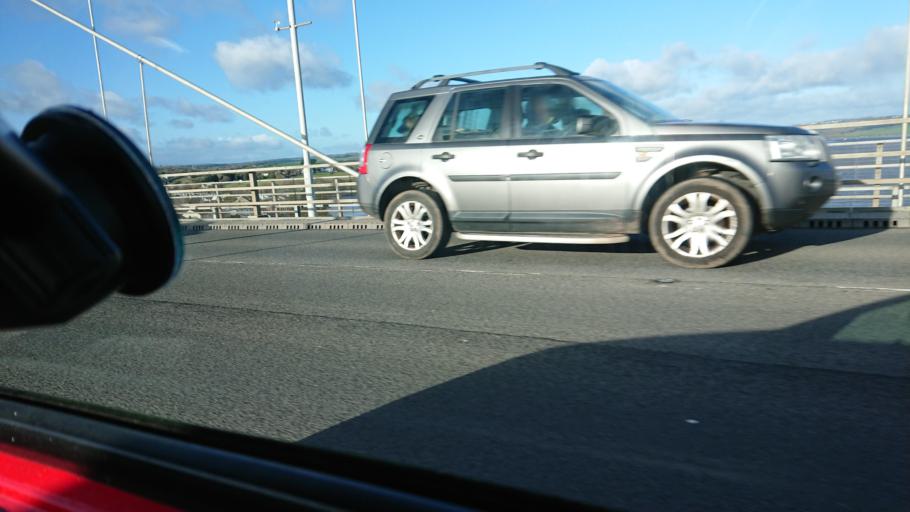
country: GB
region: England
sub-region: Cornwall
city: Saltash
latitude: 50.4082
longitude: -4.2054
